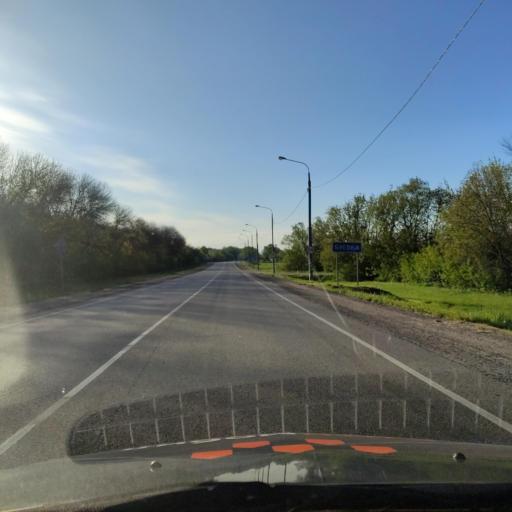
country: RU
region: Lipetsk
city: Yelets
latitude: 52.5827
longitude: 38.6278
